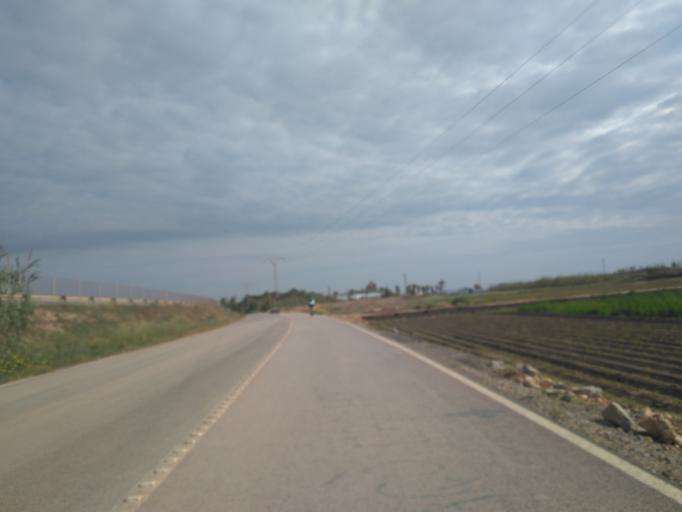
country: ES
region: Valencia
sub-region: Provincia de Valencia
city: Alboraya
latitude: 39.4984
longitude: -0.3255
